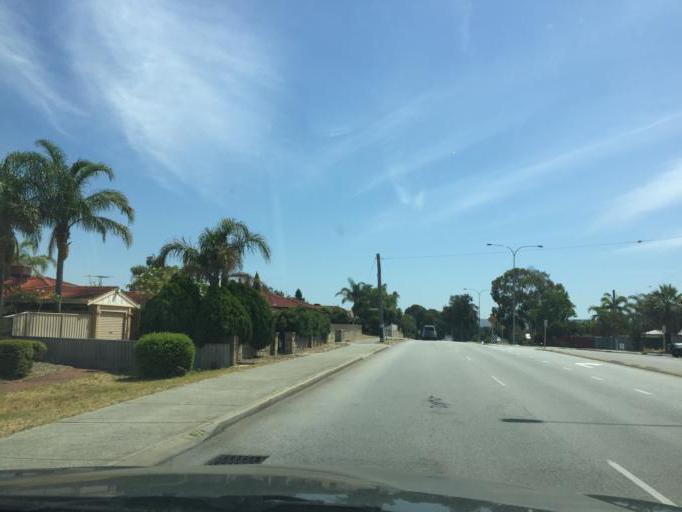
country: AU
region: Western Australia
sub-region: Gosnells
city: Thornlie
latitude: -32.0714
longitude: 115.9659
